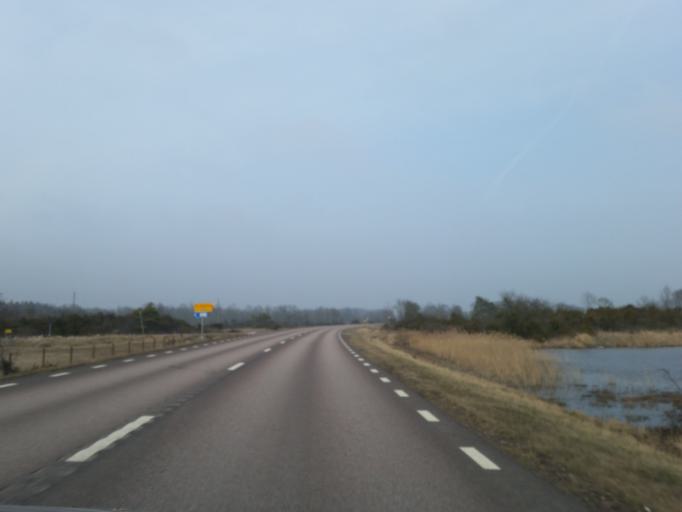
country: SE
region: Kalmar
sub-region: Borgholms Kommun
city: Borgholm
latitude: 57.1347
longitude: 16.9796
